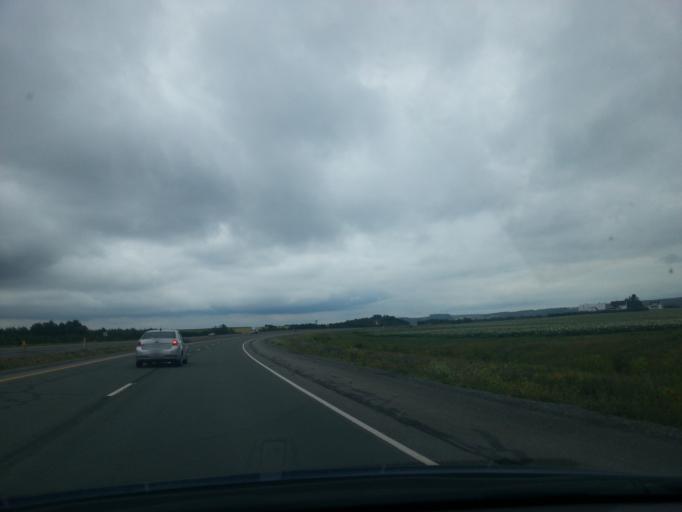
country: CA
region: New Brunswick
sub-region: Madawaska County
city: Saint-Leonard
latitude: 47.0923
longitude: -67.7805
